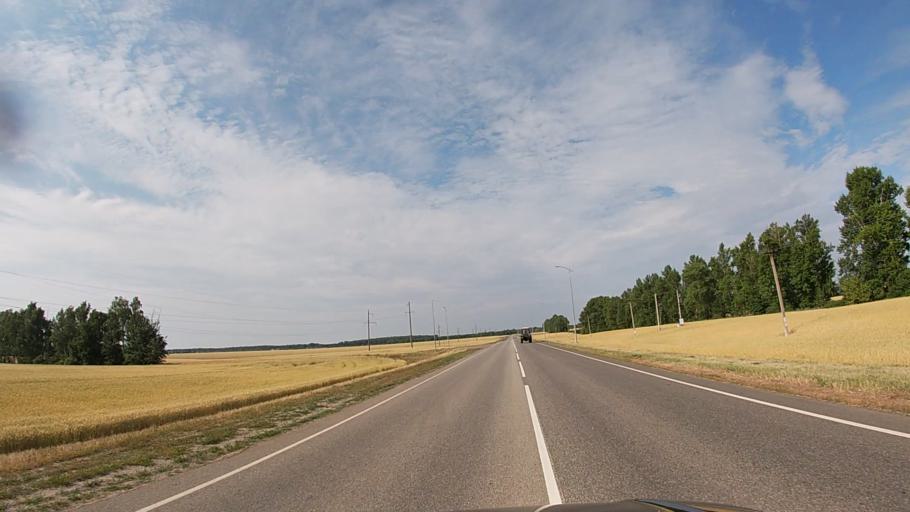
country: RU
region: Belgorod
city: Proletarskiy
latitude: 50.8140
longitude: 35.7503
